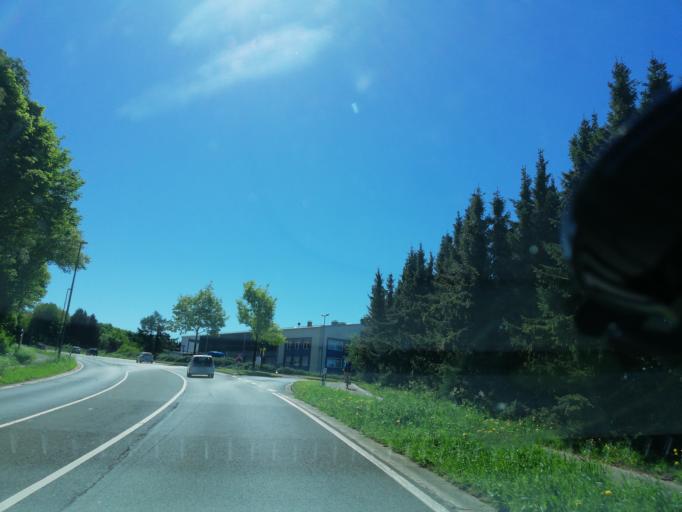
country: DE
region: North Rhine-Westphalia
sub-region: Regierungsbezirk Dusseldorf
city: Remscheid
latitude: 51.2235
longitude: 7.2363
